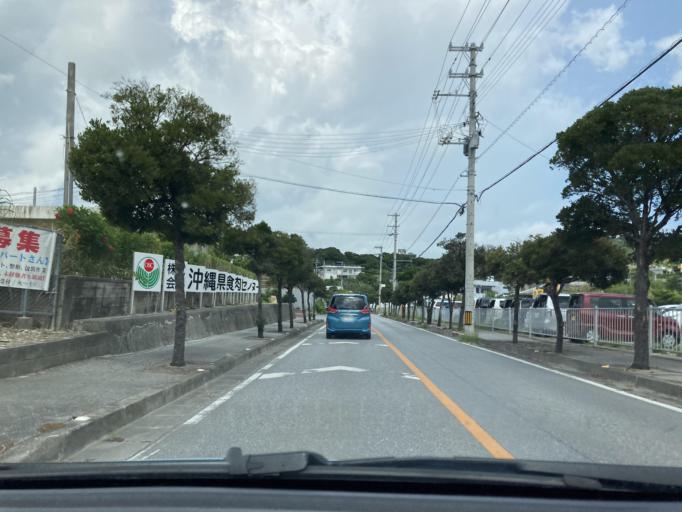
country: JP
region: Okinawa
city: Tomigusuku
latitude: 26.1689
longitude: 127.7543
